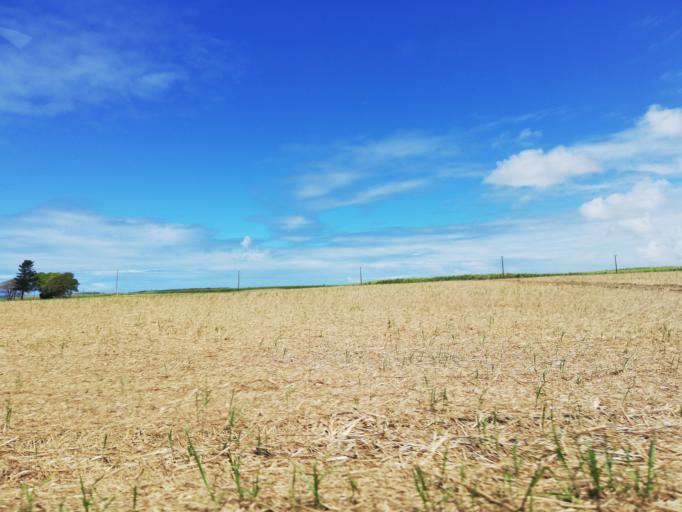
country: MU
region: Grand Port
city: Plaine Magnien
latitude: -20.4615
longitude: 57.6570
